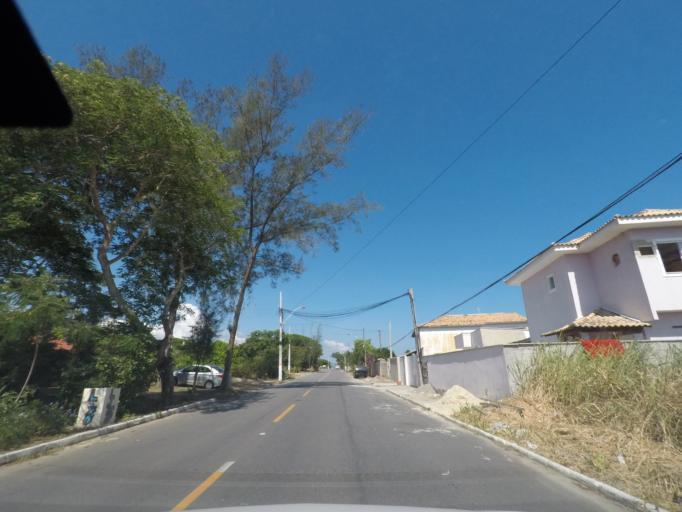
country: BR
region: Rio de Janeiro
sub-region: Marica
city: Marica
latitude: -22.9711
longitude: -42.9179
